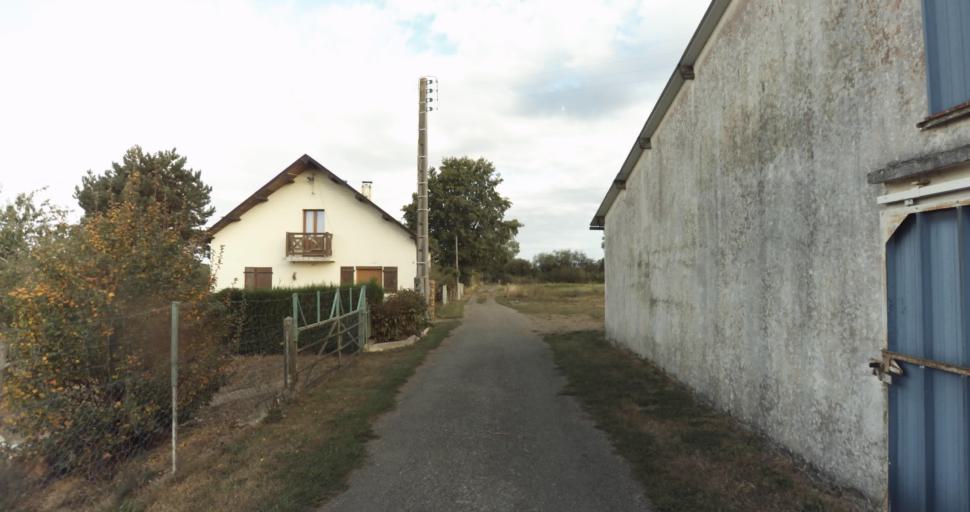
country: FR
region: Lower Normandy
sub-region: Departement de l'Orne
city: Vimoutiers
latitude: 48.9412
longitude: 0.2418
